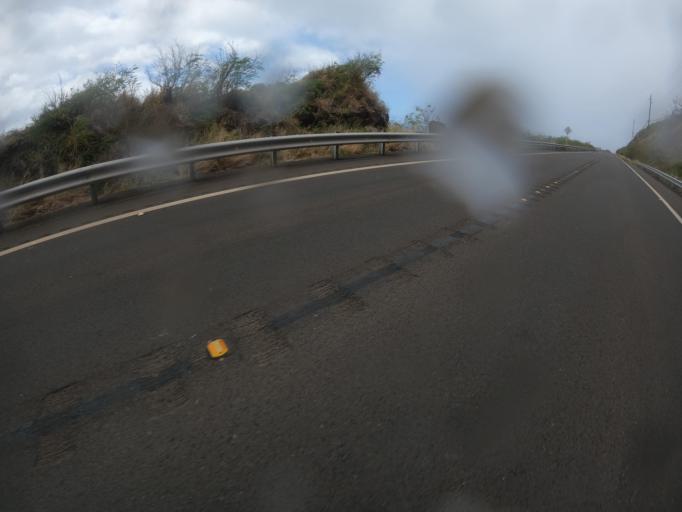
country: US
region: Hawaii
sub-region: Honolulu County
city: Makaha Valley
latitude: 21.5401
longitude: -158.2346
